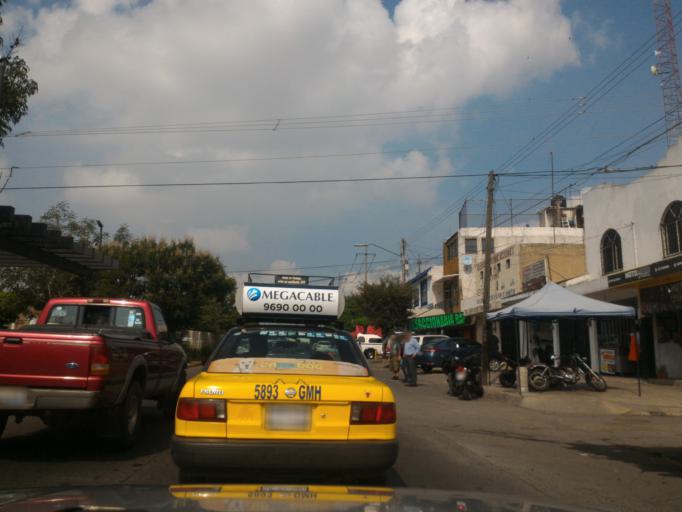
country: MX
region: Jalisco
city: Guadalajara
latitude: 20.6256
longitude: -103.3827
